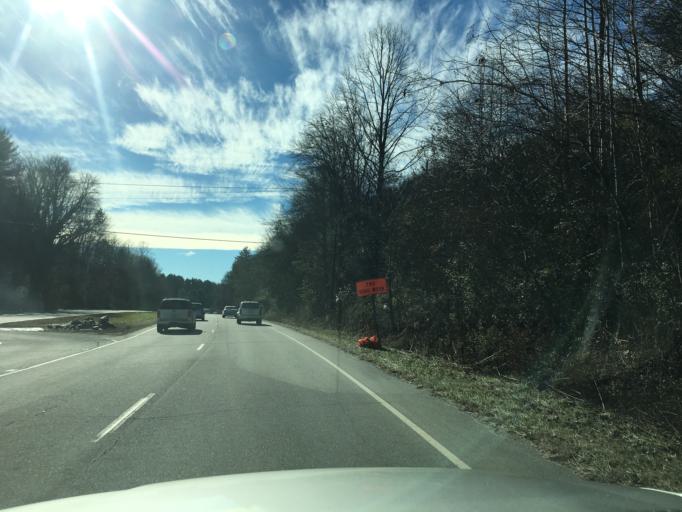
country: US
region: North Carolina
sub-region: Transylvania County
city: Brevard
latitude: 35.2678
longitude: -82.7123
